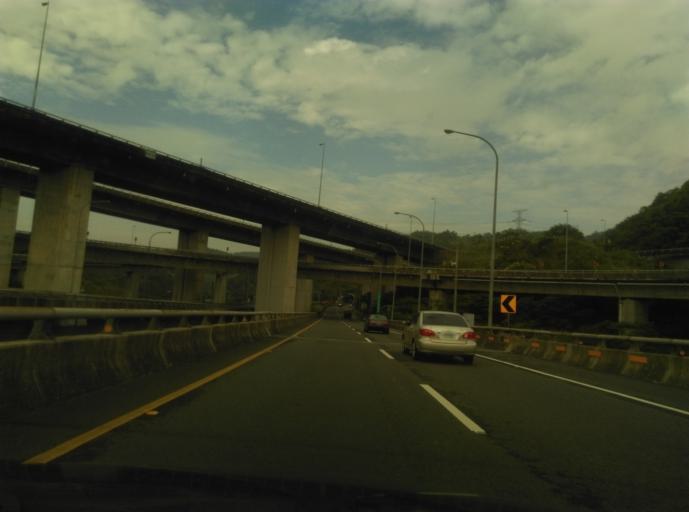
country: TW
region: Taiwan
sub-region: Keelung
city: Keelung
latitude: 25.1257
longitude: 121.6983
